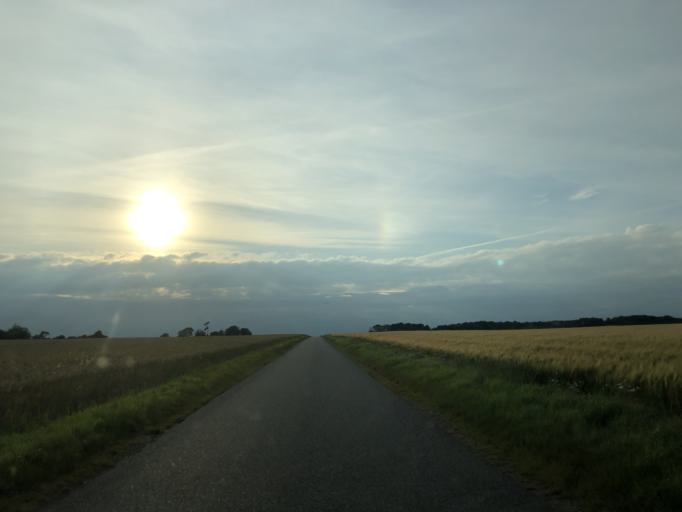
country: DK
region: South Denmark
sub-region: Fredericia Kommune
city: Taulov
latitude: 55.5939
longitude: 9.6130
